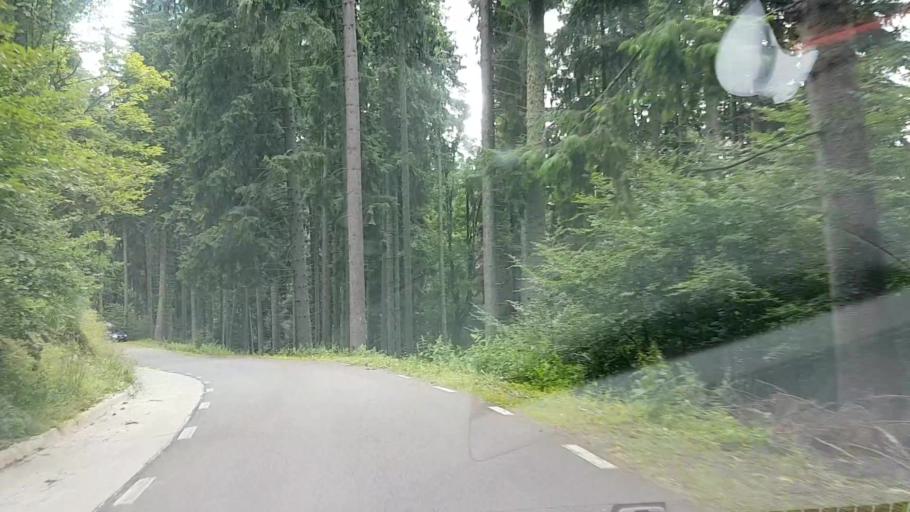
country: RO
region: Suceava
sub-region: Comuna Crucea
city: Crucea
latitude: 47.4344
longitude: 25.5697
